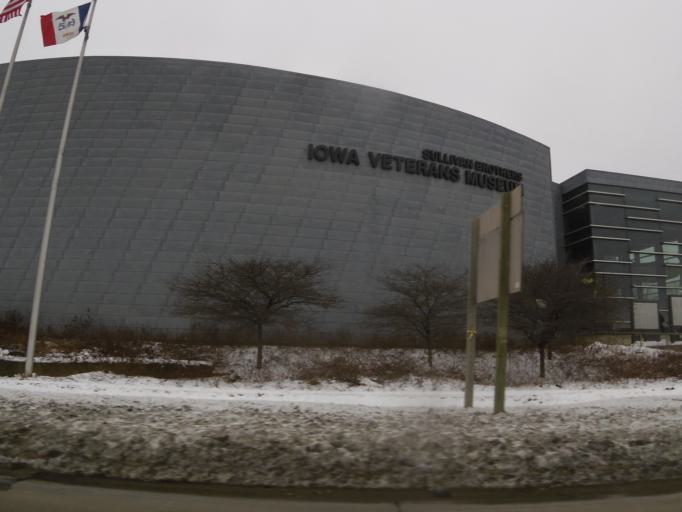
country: US
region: Iowa
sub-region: Black Hawk County
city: Waterloo
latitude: 42.4933
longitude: -92.3434
